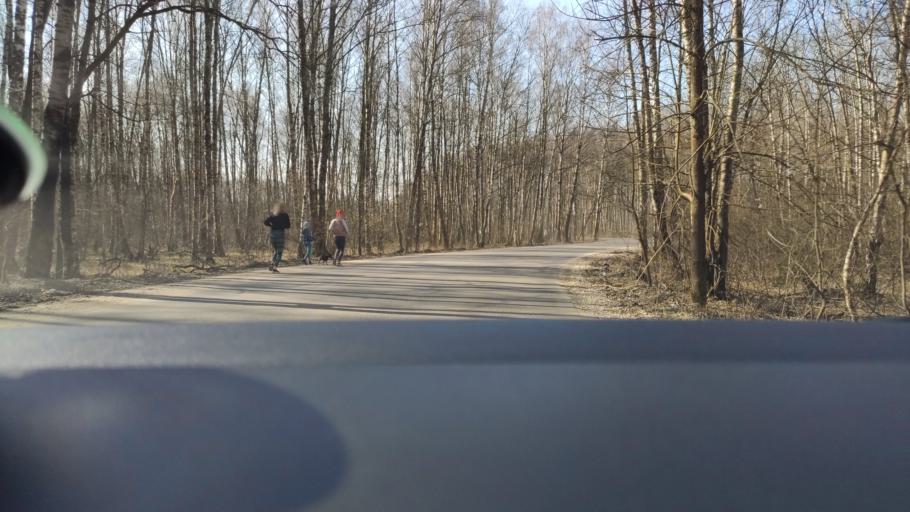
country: RU
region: Moskovskaya
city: Elektrostal'
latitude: 55.7679
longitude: 38.4048
